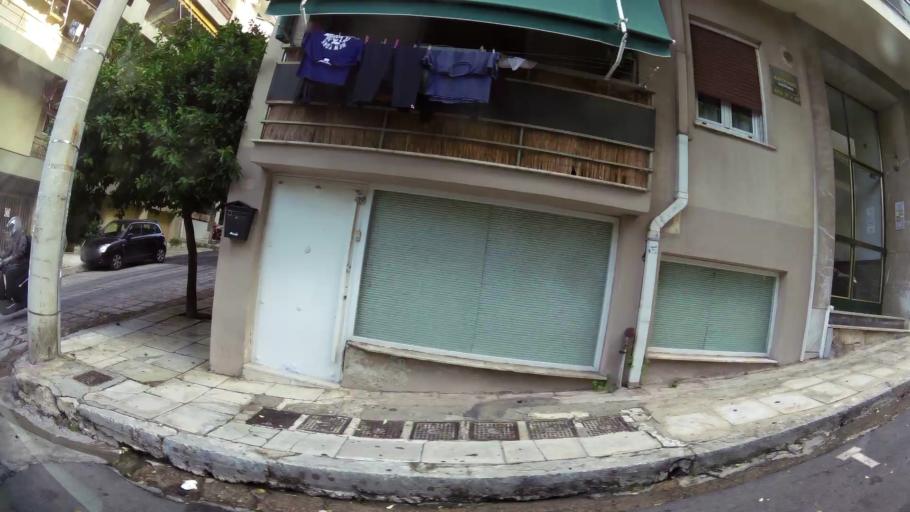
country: GR
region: Attica
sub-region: Nomarchia Athinas
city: Kaisariani
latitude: 37.9735
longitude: 23.7676
